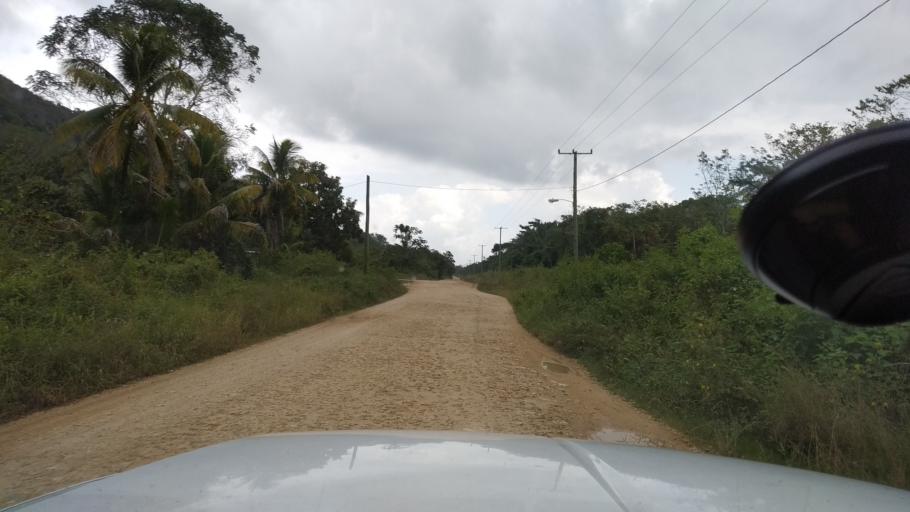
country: BZ
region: Toledo
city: Punta Gorda
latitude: 16.2127
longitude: -89.0172
